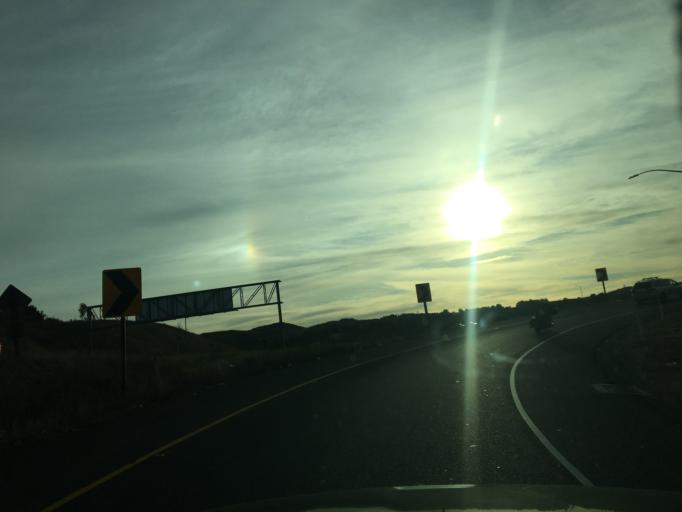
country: US
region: California
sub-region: Orange County
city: Laguna Woods
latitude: 33.6504
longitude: -117.7602
